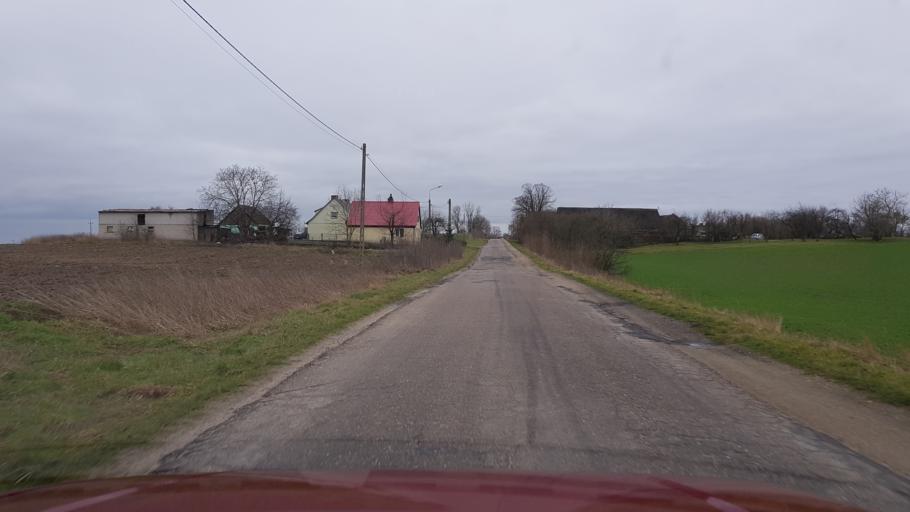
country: PL
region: West Pomeranian Voivodeship
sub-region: Powiat koszalinski
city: Mielno
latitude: 54.1840
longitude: 16.0181
